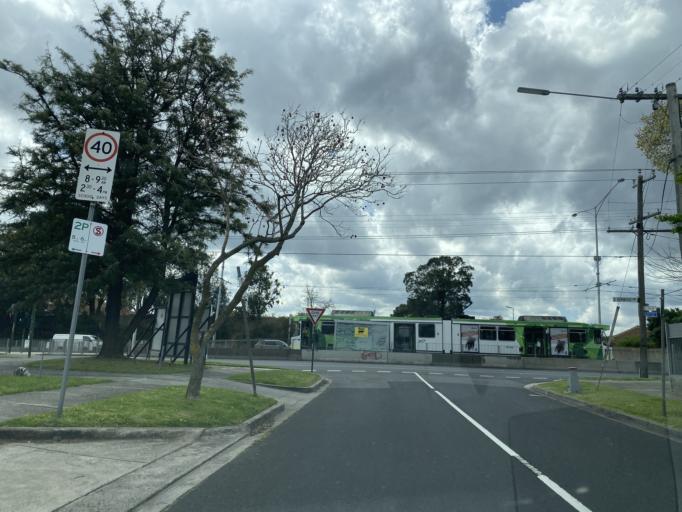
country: AU
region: Victoria
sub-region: Whitehorse
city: Burwood
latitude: -37.8518
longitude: 145.1264
